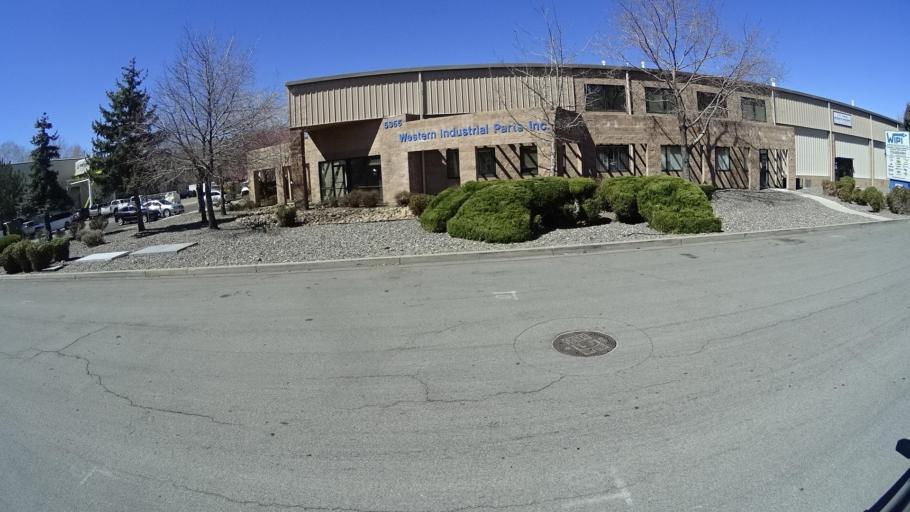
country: US
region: Nevada
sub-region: Washoe County
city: Sparks
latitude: 39.4727
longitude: -119.7692
